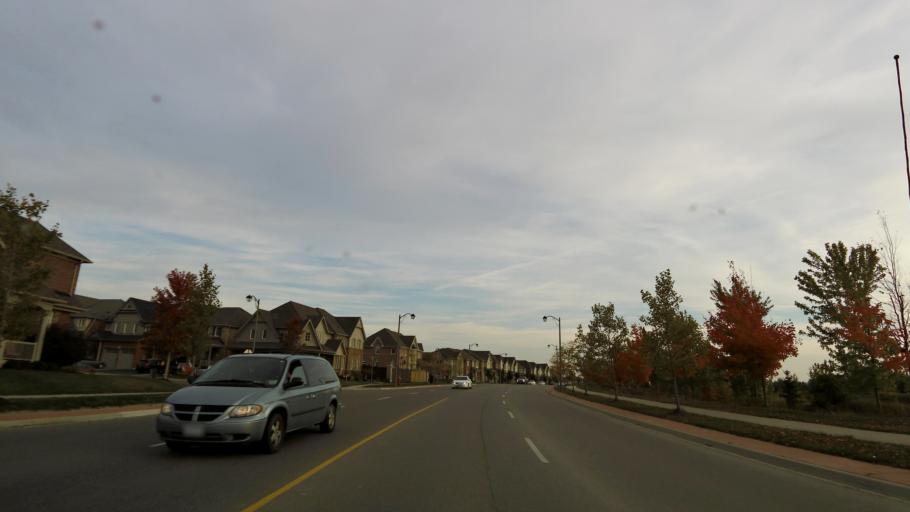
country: CA
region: Ontario
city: Brampton
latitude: 43.7536
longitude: -79.8235
